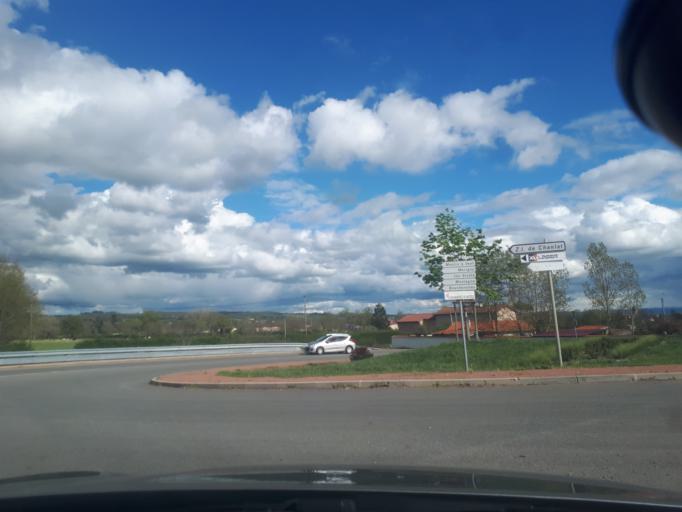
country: FR
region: Rhone-Alpes
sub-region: Departement de la Loire
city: Balbigny
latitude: 45.8267
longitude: 4.1764
